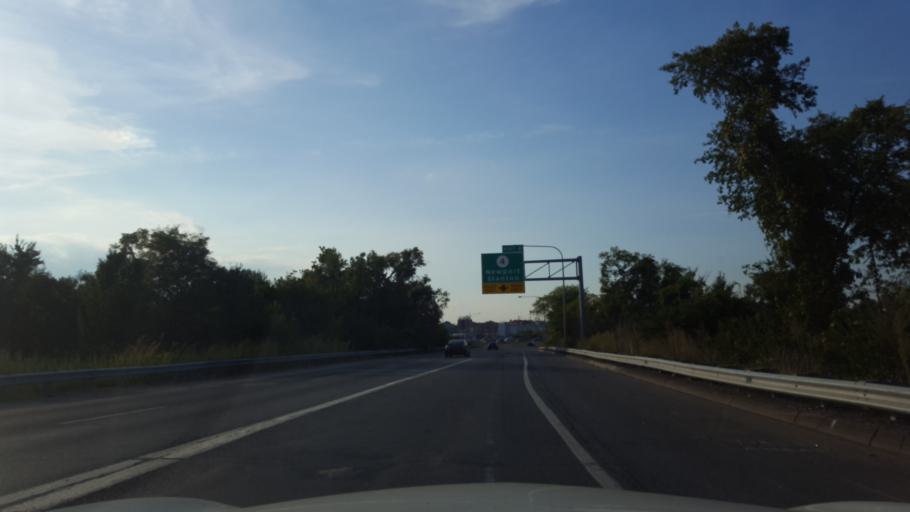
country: US
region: Delaware
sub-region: New Castle County
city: Newport
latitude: 39.7065
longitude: -75.6053
